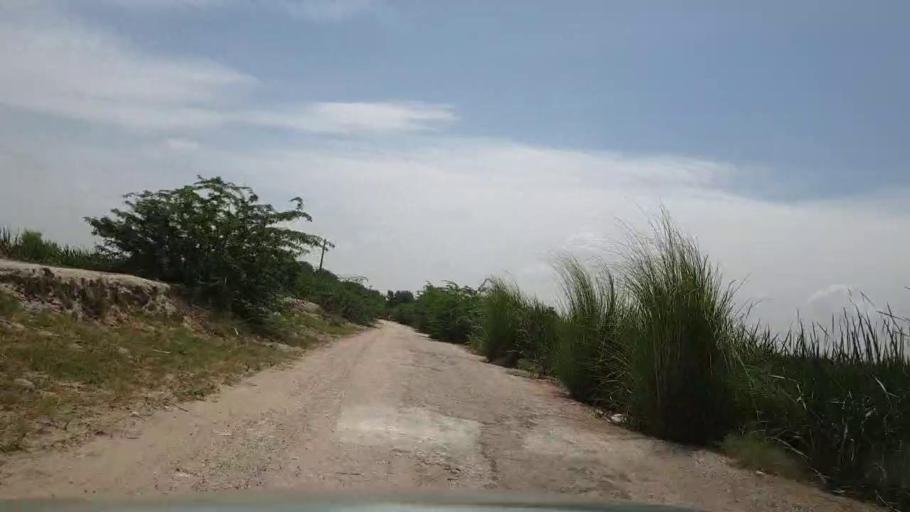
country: PK
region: Sindh
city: Bozdar
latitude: 27.0774
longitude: 68.9679
